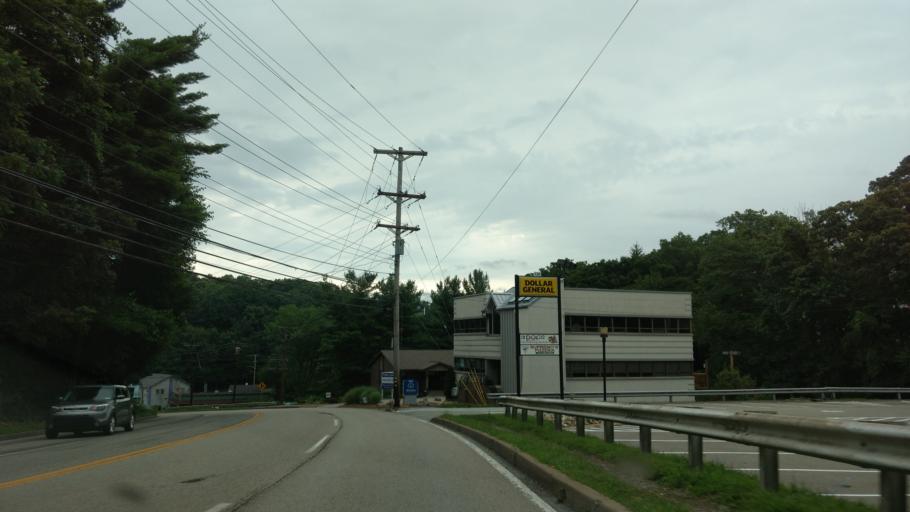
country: US
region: Pennsylvania
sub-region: Allegheny County
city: West View
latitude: 40.5443
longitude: -80.0332
